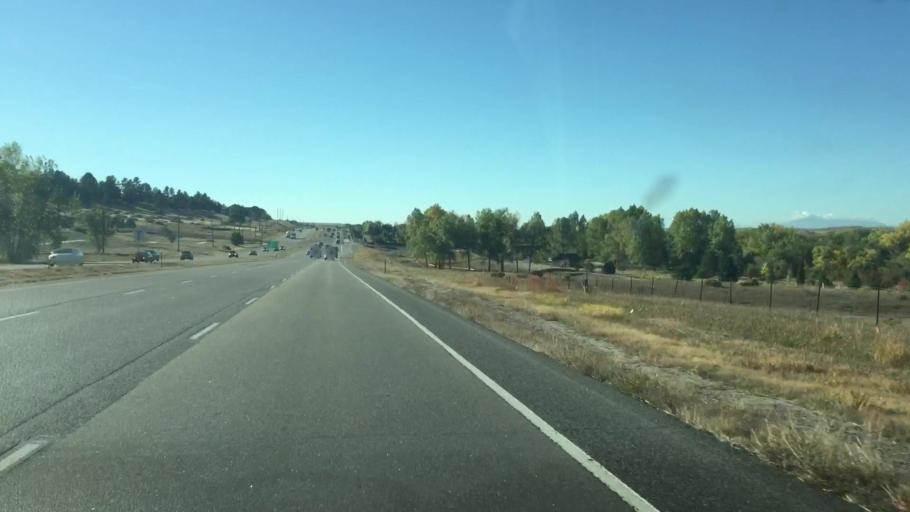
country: US
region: Colorado
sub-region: Douglas County
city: Parker
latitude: 39.5046
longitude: -104.7628
